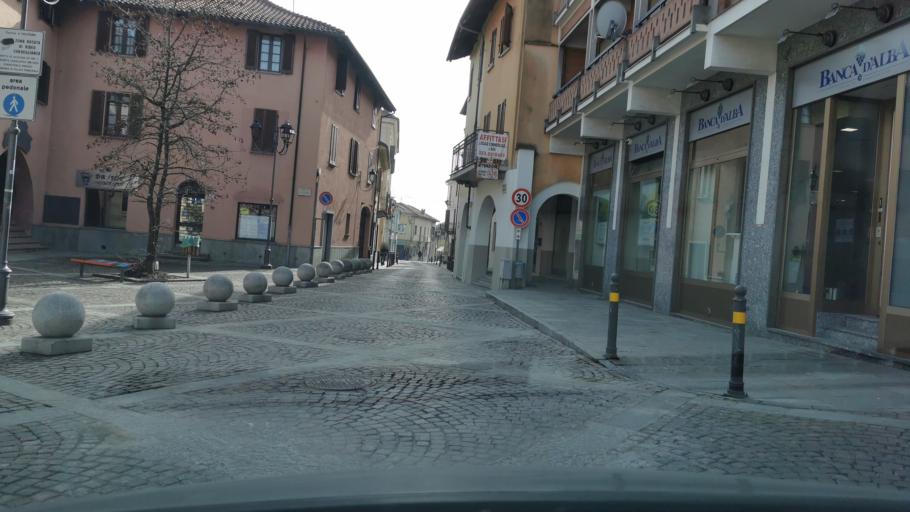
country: IT
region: Piedmont
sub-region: Provincia di Torino
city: Volpiano
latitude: 45.2017
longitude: 7.7753
